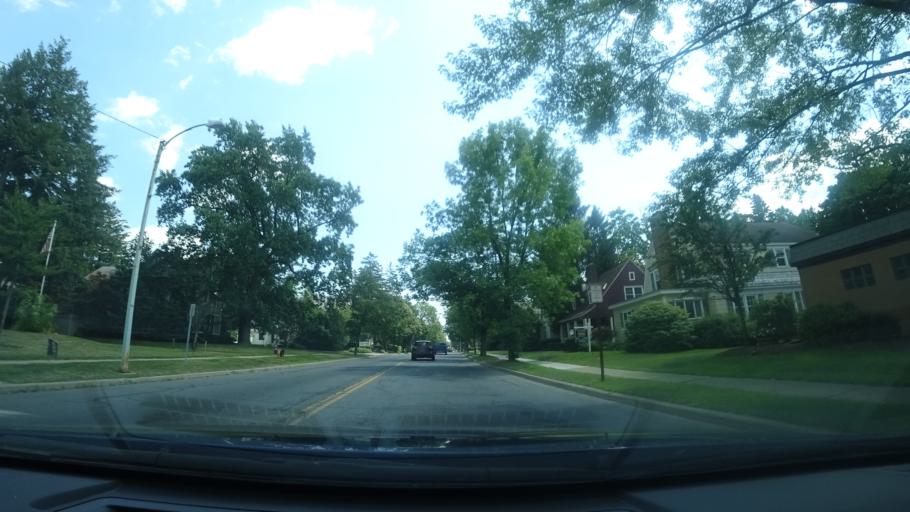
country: US
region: New York
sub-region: Warren County
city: Glens Falls
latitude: 43.3162
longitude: -73.6540
